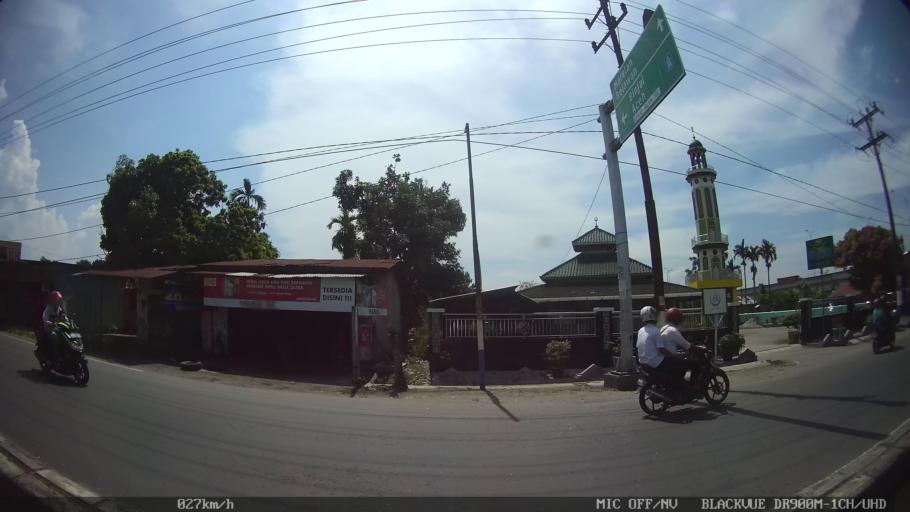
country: ID
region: North Sumatra
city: Medan
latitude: 3.6496
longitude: 98.6572
